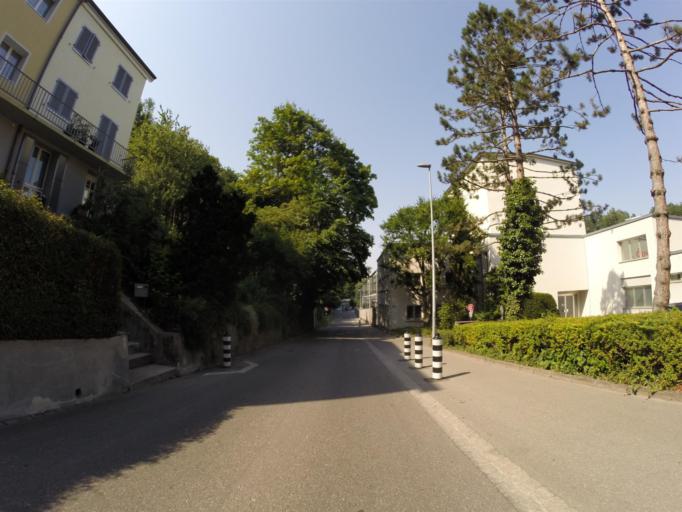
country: CH
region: Bern
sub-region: Bern-Mittelland District
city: Bern
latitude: 46.9601
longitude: 7.4414
